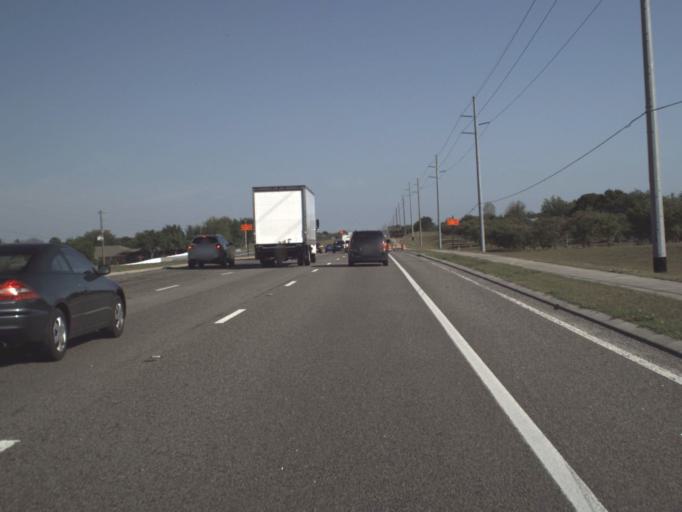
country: US
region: Florida
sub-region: Lake County
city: Four Corners
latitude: 28.3889
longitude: -81.6912
